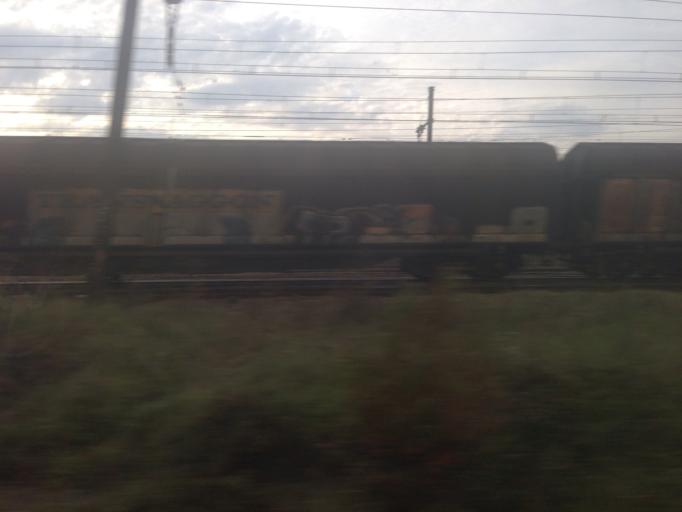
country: FR
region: Ile-de-France
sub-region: Departement de l'Essonne
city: Athis-Mons
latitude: 48.6974
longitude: 2.3901
